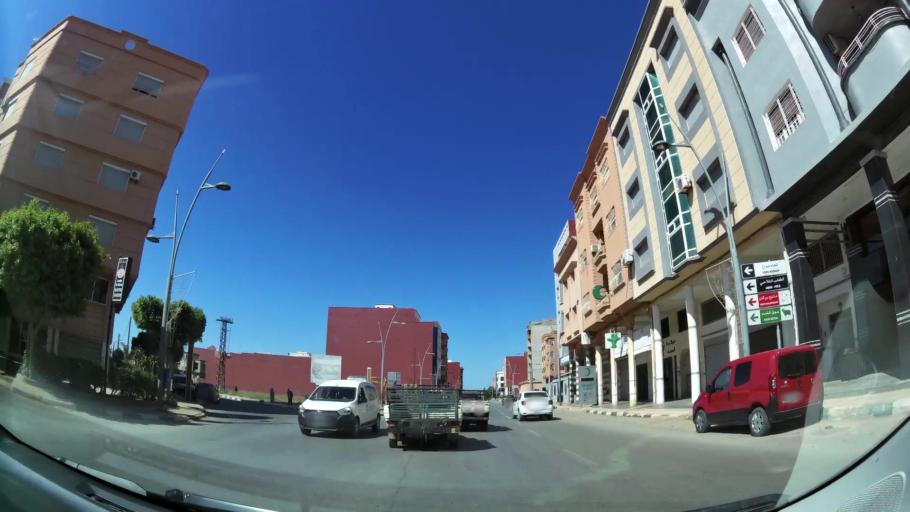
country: MA
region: Oriental
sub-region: Berkane-Taourirt
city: Berkane
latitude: 34.9357
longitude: -2.3236
